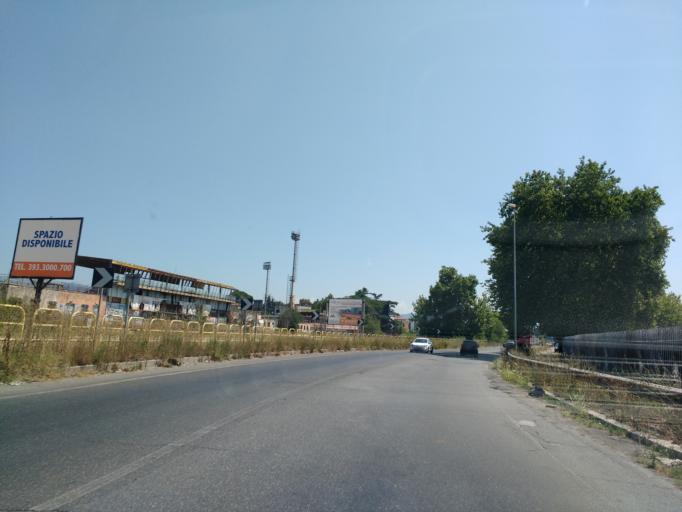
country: IT
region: Latium
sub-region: Citta metropolitana di Roma Capitale
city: Albuccione
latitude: 41.9517
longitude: 12.6876
